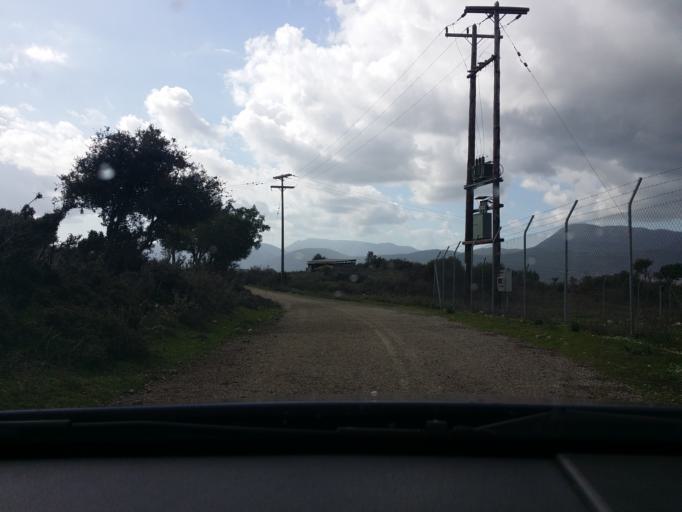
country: GR
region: West Greece
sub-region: Nomos Aitolias kai Akarnanias
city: Fitiai
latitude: 38.6727
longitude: 21.1910
